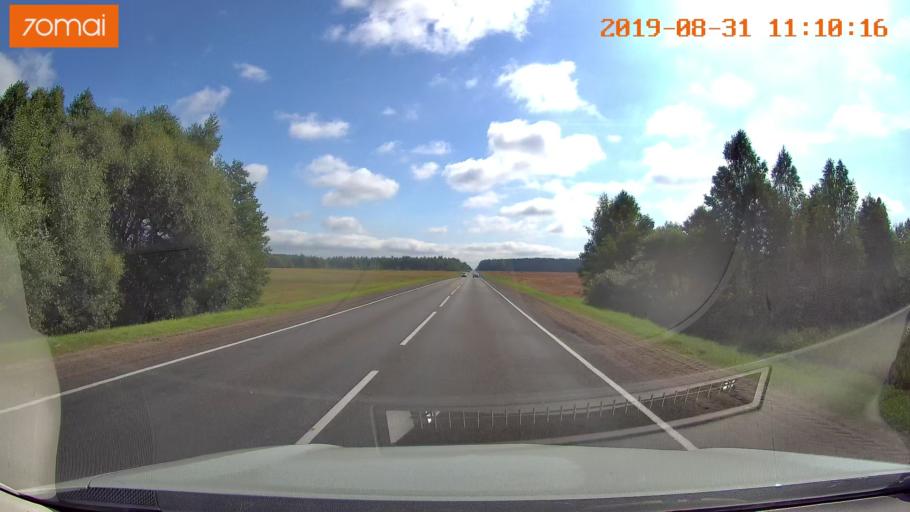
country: BY
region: Mogilev
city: Ramanavichy
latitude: 53.8218
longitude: 30.7270
